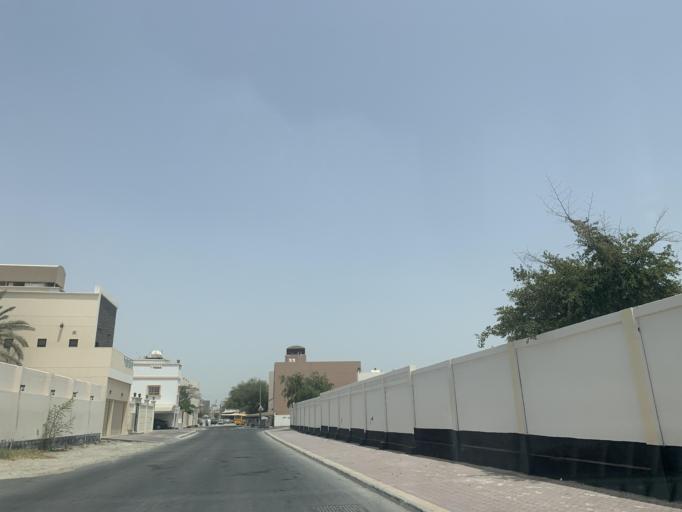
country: BH
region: Northern
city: Madinat `Isa
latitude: 26.1525
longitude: 50.5231
